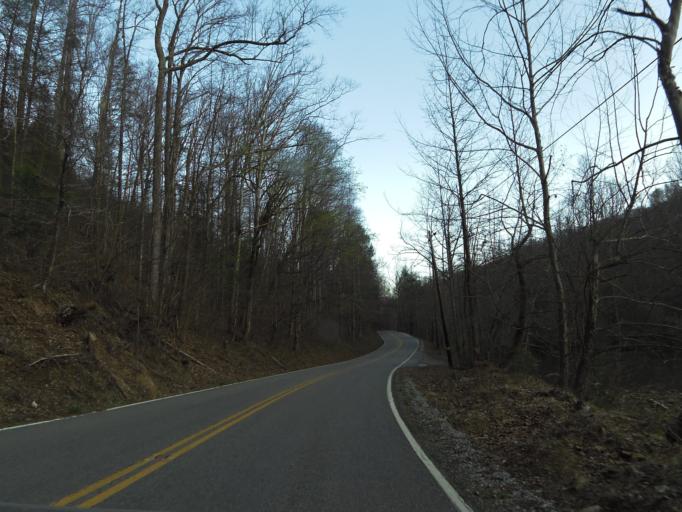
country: US
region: Tennessee
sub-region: Campbell County
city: Caryville
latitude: 36.2025
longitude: -84.3047
